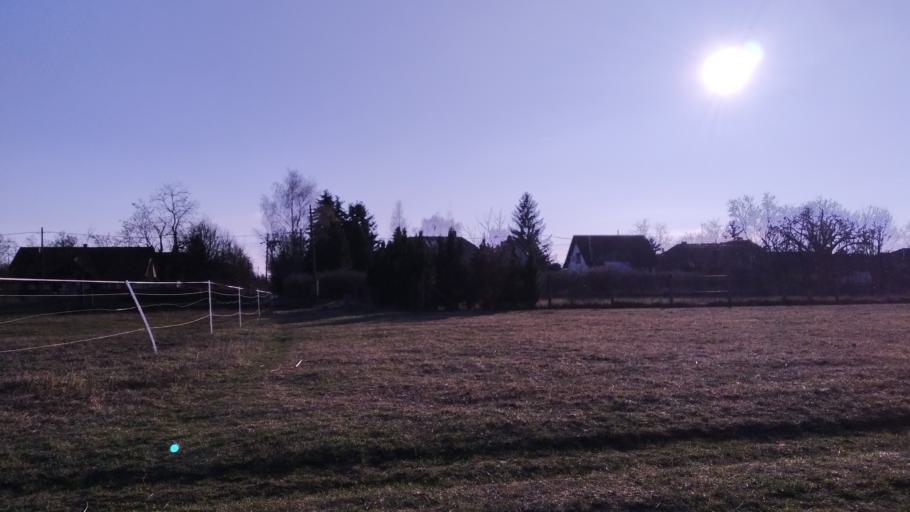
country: HU
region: Pest
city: Budakalasz
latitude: 47.6332
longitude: 19.0503
